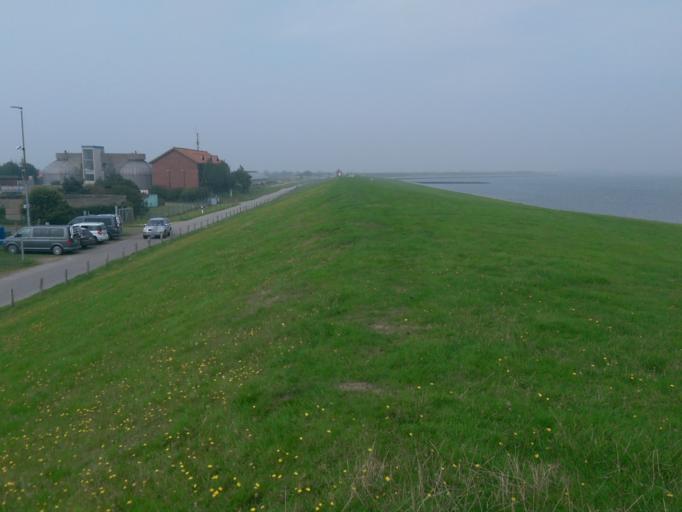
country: DE
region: Schleswig-Holstein
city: Wyk auf Fohr
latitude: 54.6961
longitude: 8.5750
